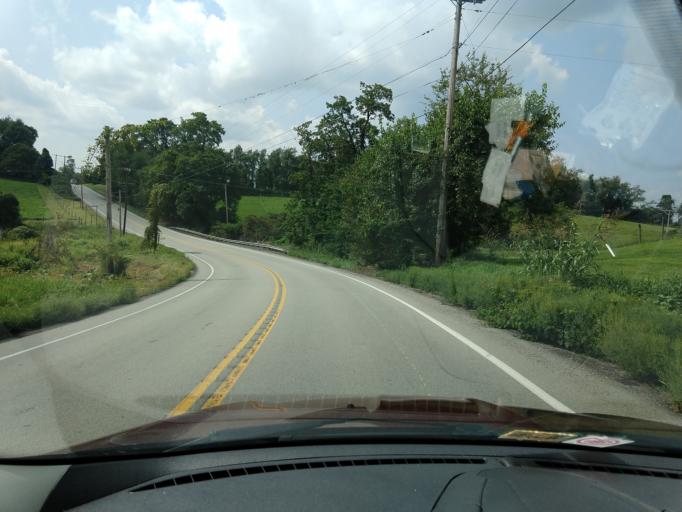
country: US
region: Pennsylvania
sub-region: Washington County
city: Ellsworth
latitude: 40.1870
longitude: -80.0556
